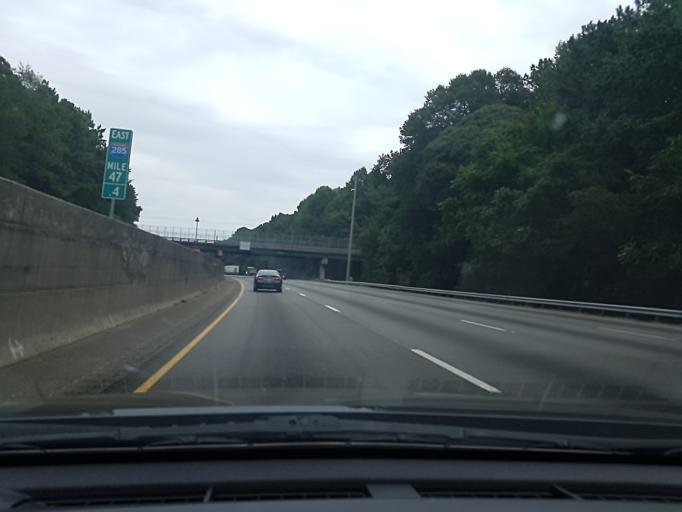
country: US
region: Georgia
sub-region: DeKalb County
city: Panthersville
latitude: 33.7009
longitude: -84.2531
